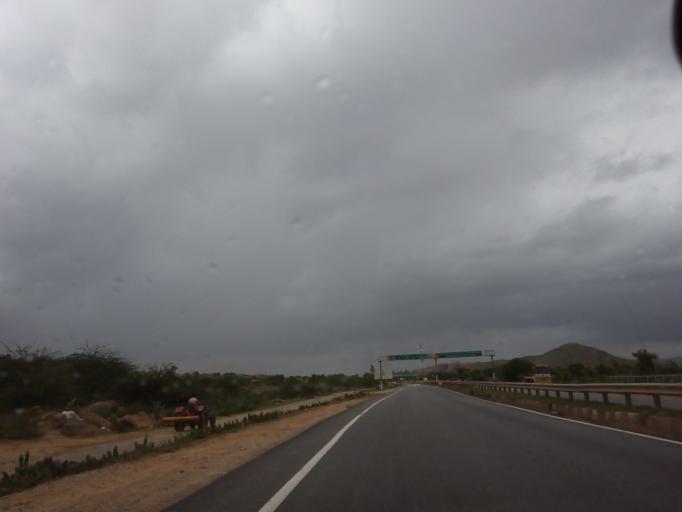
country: IN
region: Karnataka
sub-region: Chitradurga
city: Chitradurga
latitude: 14.2630
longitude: 76.3438
